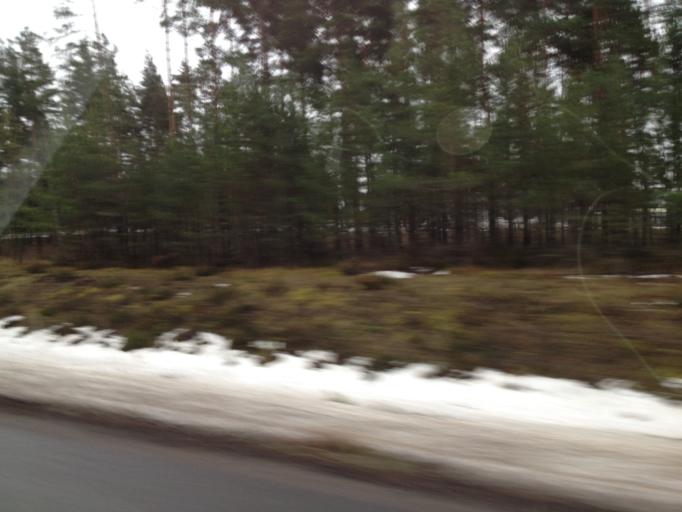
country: FI
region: Uusimaa
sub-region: Raaseporin
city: Hanko
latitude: 59.8564
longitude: 23.0216
